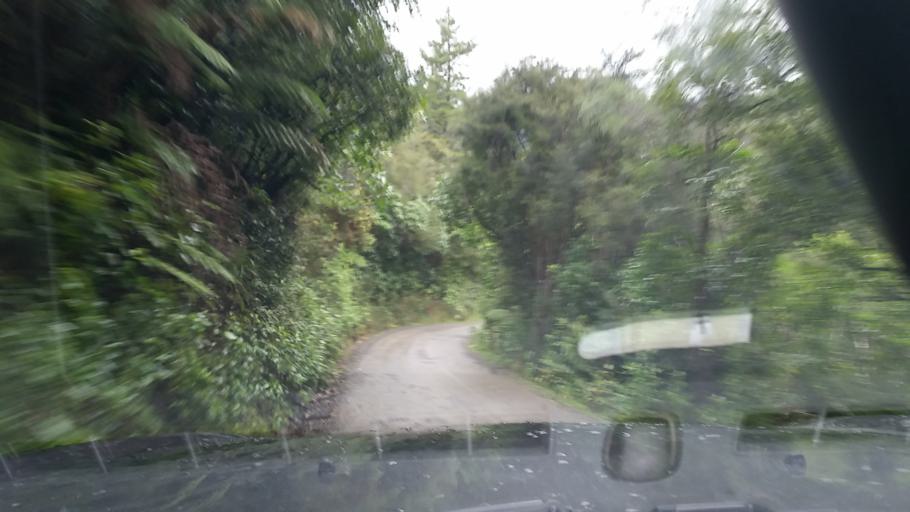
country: NZ
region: Marlborough
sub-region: Marlborough District
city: Picton
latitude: -41.2869
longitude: 174.0372
